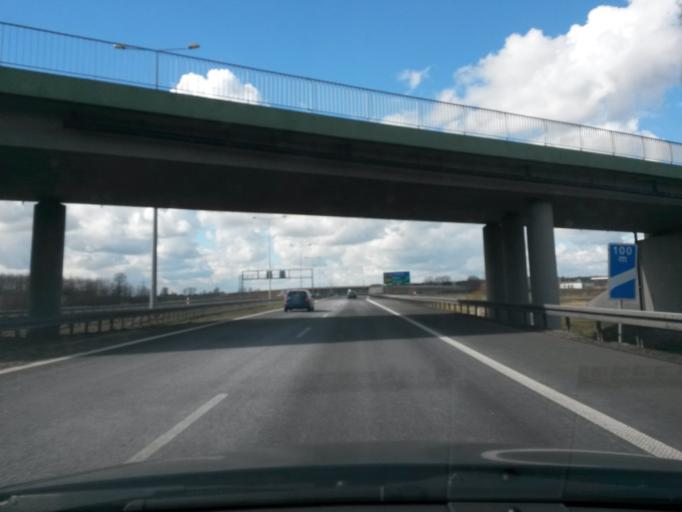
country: PL
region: Greater Poland Voivodeship
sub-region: Powiat kolski
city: Dabie
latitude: 52.0673
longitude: 18.8225
